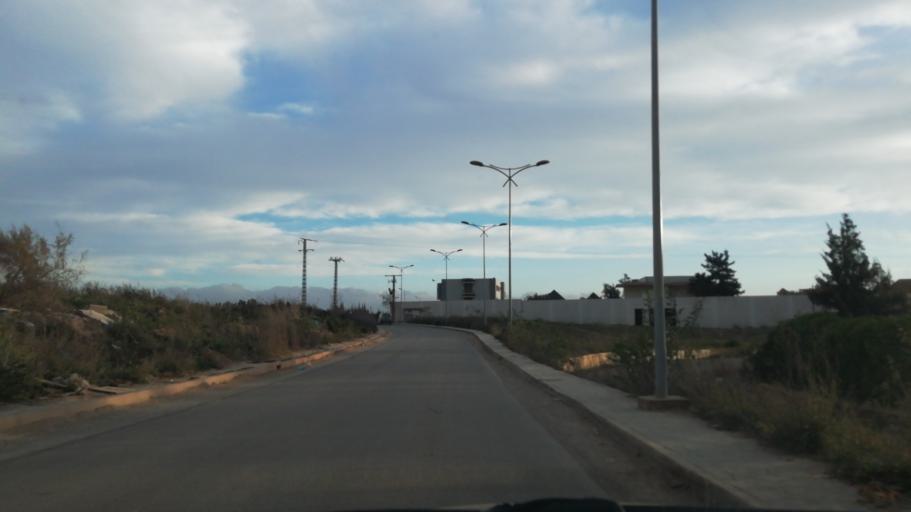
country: DZ
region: Oran
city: Es Senia
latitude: 35.6860
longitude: -0.5876
